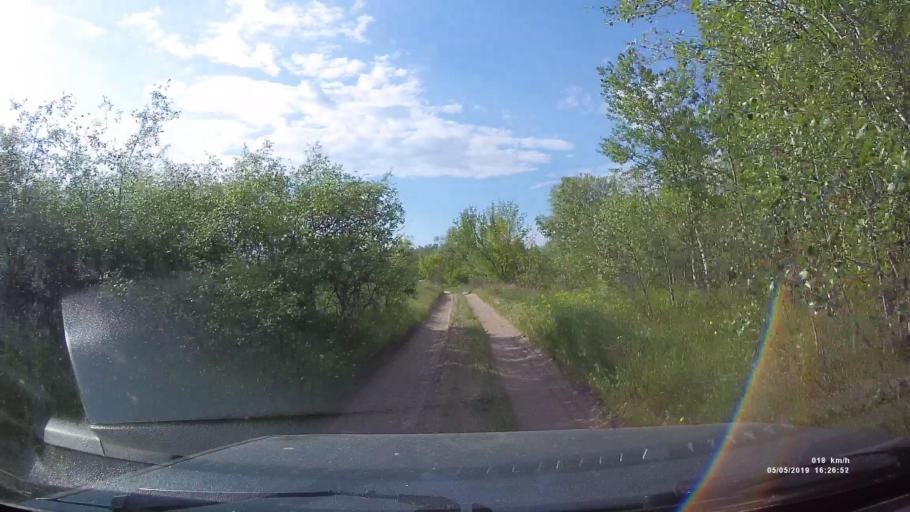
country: RU
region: Rostov
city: Ust'-Donetskiy
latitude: 47.7638
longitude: 41.0207
